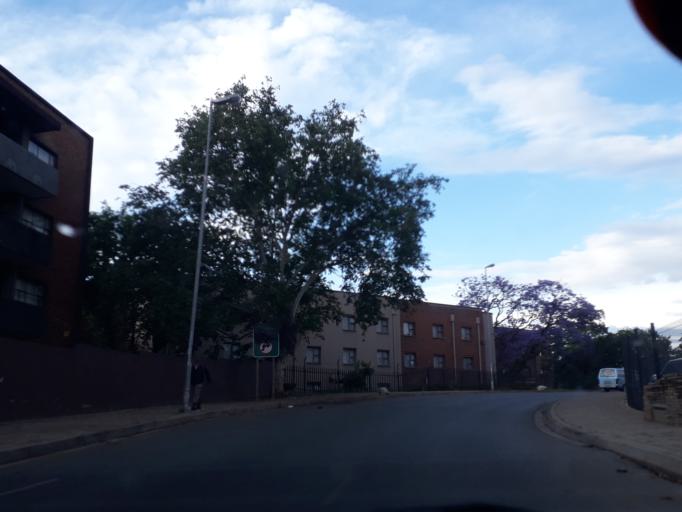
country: ZA
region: Gauteng
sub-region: City of Johannesburg Metropolitan Municipality
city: Johannesburg
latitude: -26.1825
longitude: 28.0482
